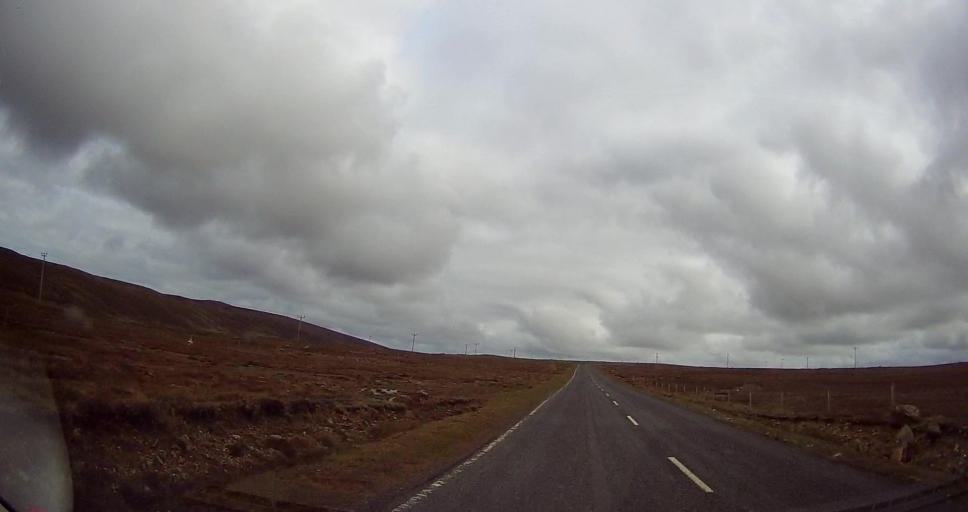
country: GB
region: Scotland
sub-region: Shetland Islands
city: Shetland
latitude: 60.7165
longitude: -0.9136
